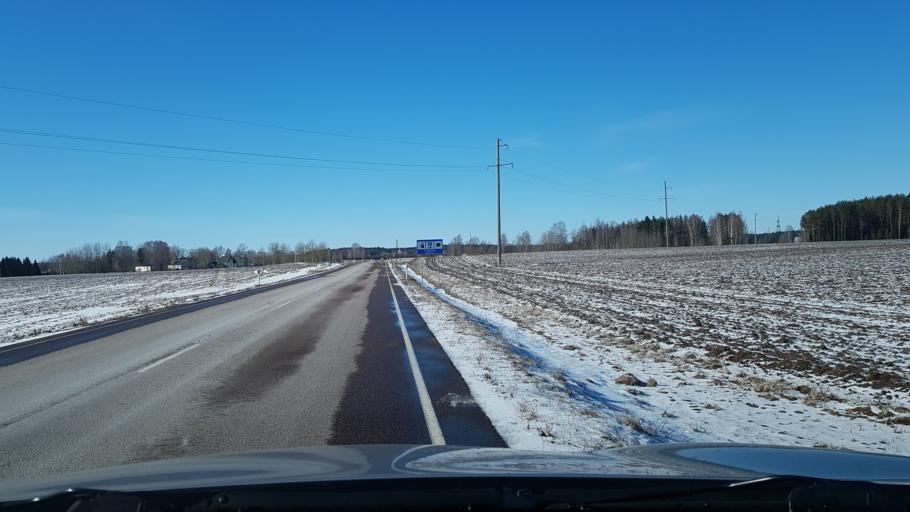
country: EE
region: Polvamaa
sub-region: Polva linn
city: Polva
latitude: 58.0896
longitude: 27.1000
